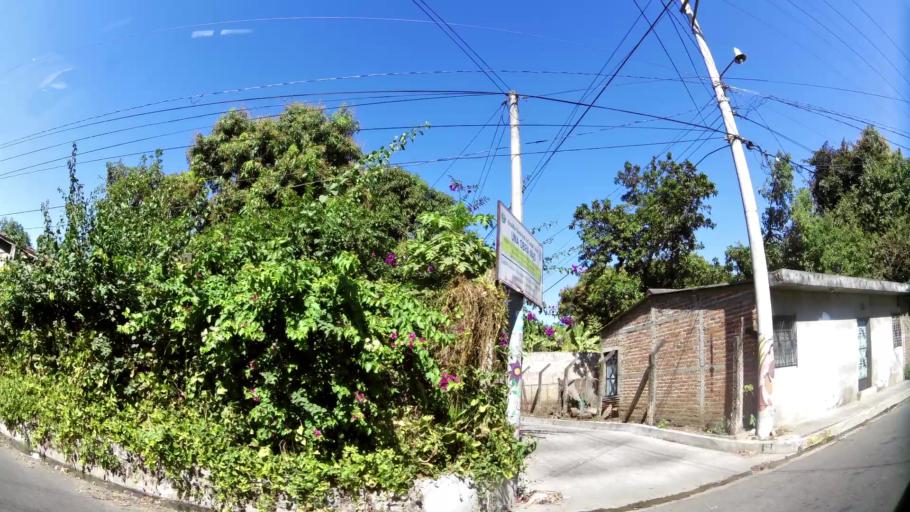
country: SV
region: La Libertad
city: Santa Tecla
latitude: 13.7318
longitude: -89.3724
